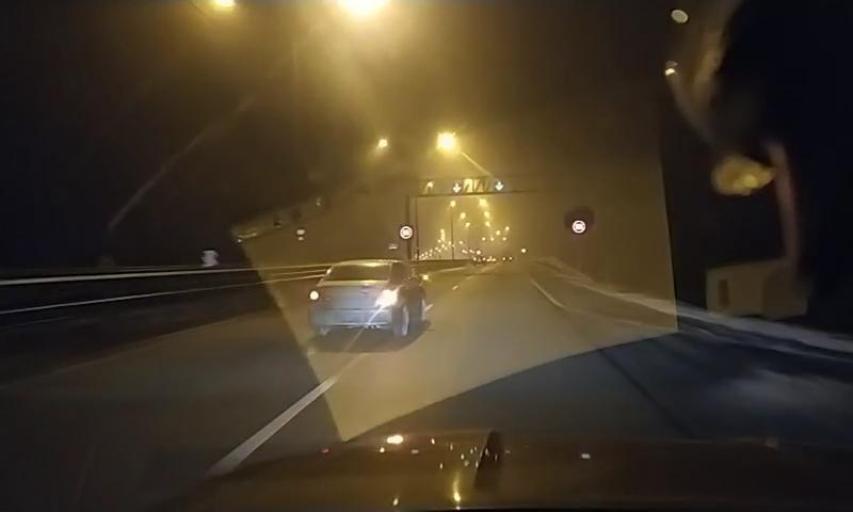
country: RU
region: Leningrad
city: Bugry
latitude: 60.1146
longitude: 30.3864
